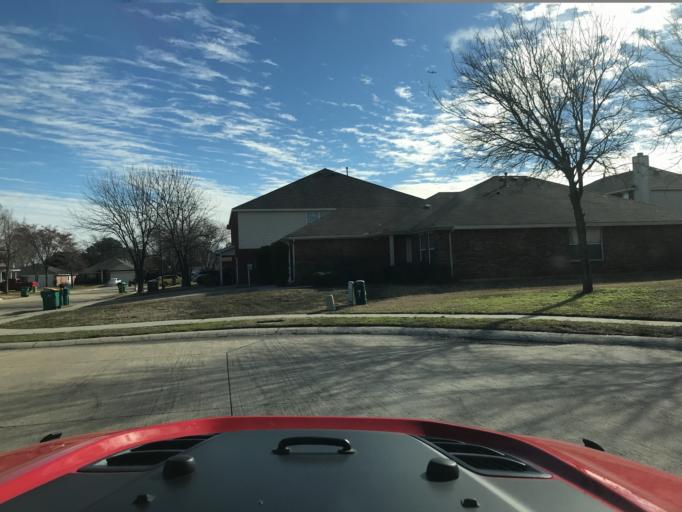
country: US
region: Texas
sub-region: Denton County
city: Lewisville
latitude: 33.0476
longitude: -97.0332
